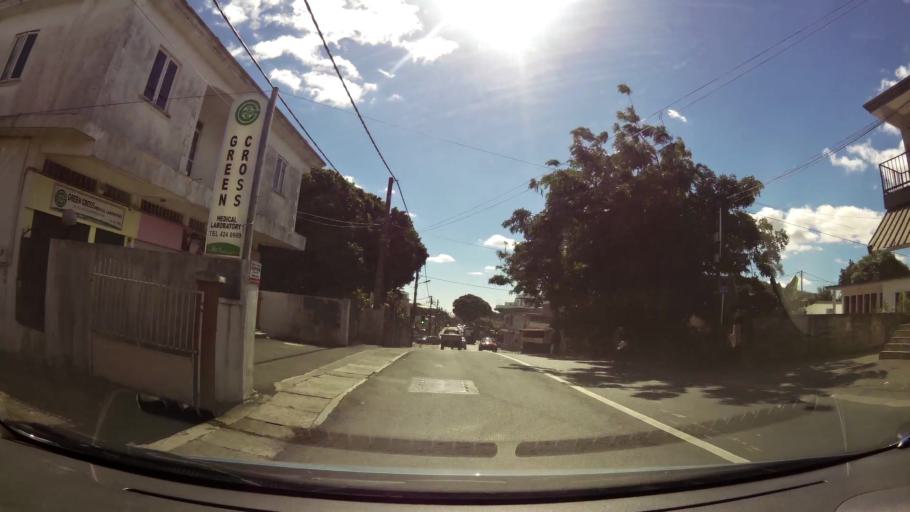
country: MU
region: Plaines Wilhems
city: Vacoas
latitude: -20.2856
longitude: 57.4803
